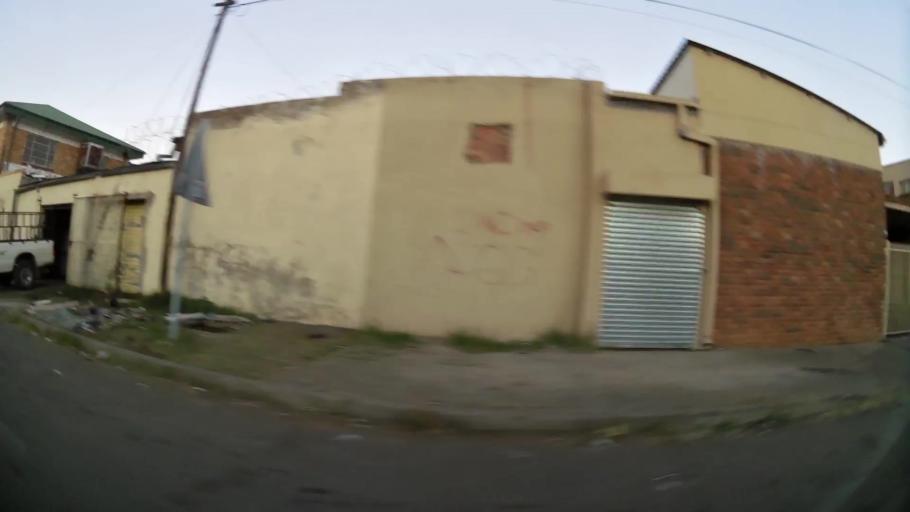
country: ZA
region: Northern Cape
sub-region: Frances Baard District Municipality
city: Kimberley
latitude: -28.7280
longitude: 24.7663
